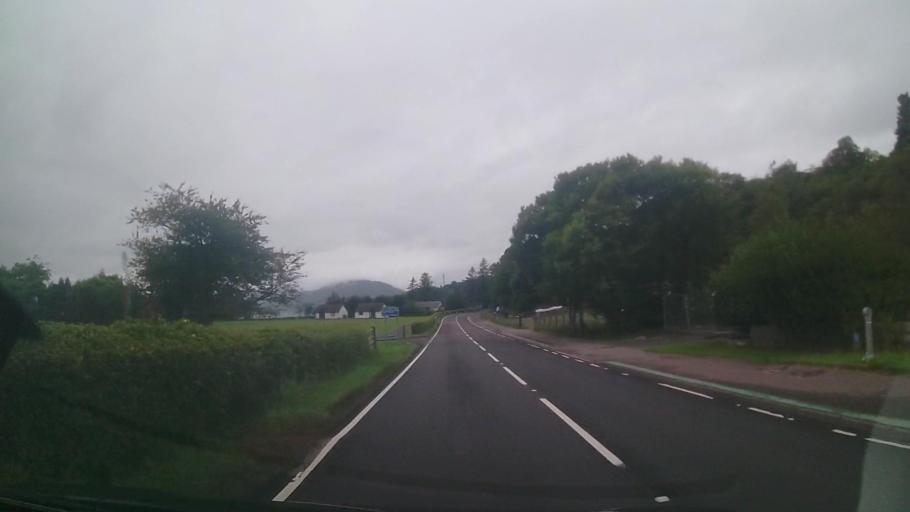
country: GB
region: Scotland
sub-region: Highland
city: Fort William
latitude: 56.7027
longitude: -5.2264
